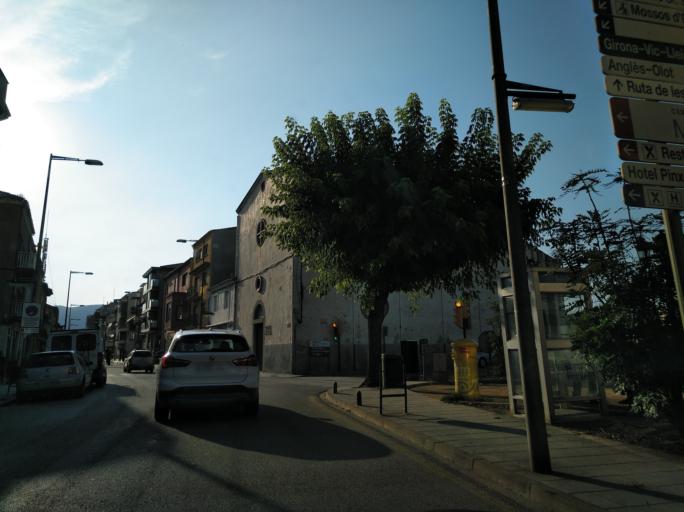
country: ES
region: Catalonia
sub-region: Provincia de Girona
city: Santa Coloma de Farners
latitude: 41.8607
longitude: 2.6680
